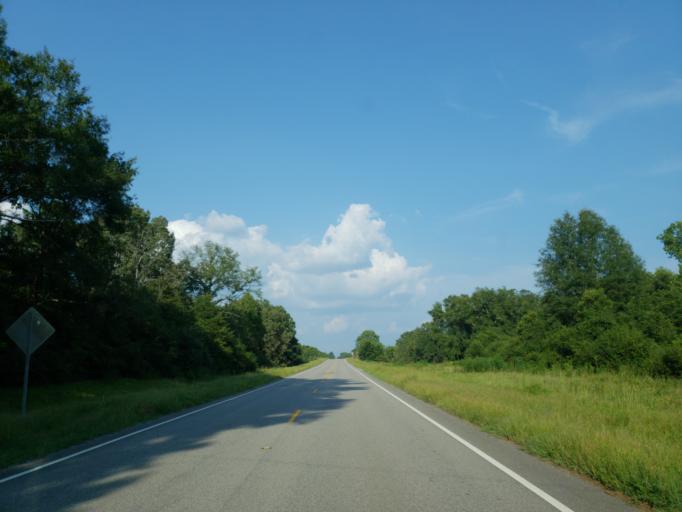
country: US
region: Alabama
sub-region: Greene County
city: Eutaw
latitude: 32.7558
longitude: -88.0256
